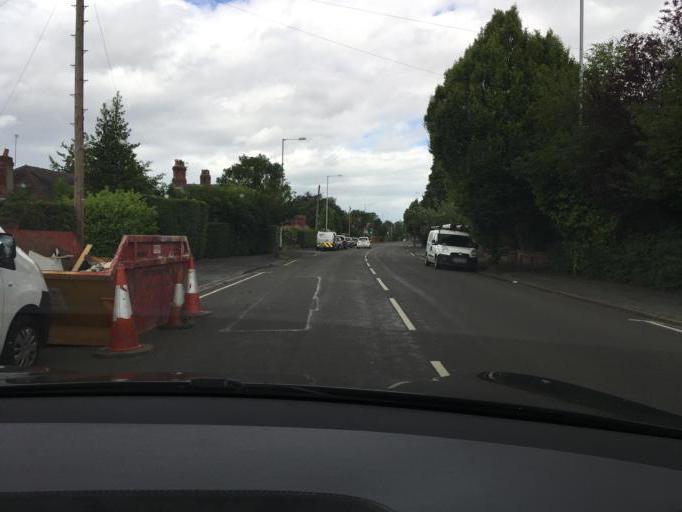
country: GB
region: England
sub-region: Borough of Stockport
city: Hazel Grove
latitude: 53.3708
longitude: -2.1242
